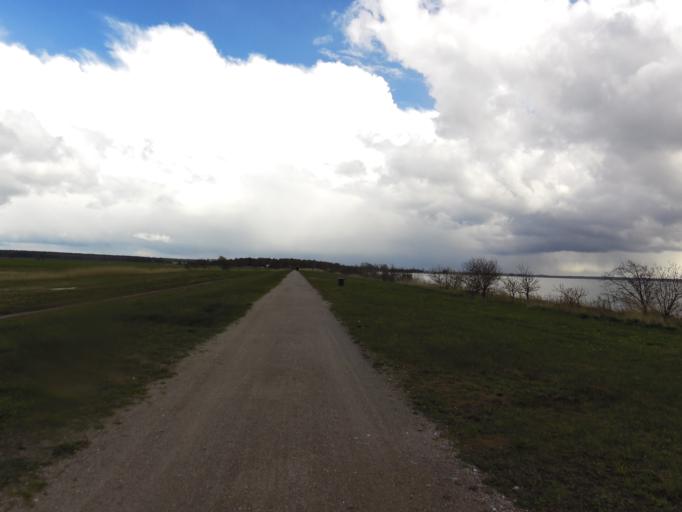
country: DE
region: Mecklenburg-Vorpommern
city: Born
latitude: 54.3823
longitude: 12.4837
